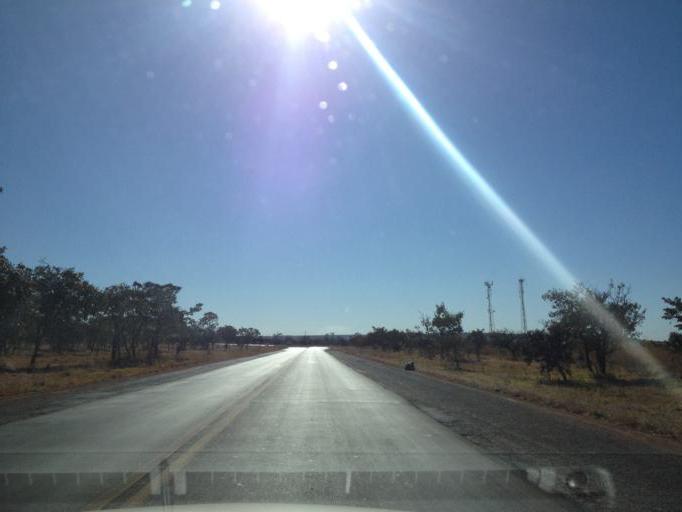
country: BR
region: Federal District
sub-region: Brasilia
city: Brasilia
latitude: -15.6959
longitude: -47.8315
